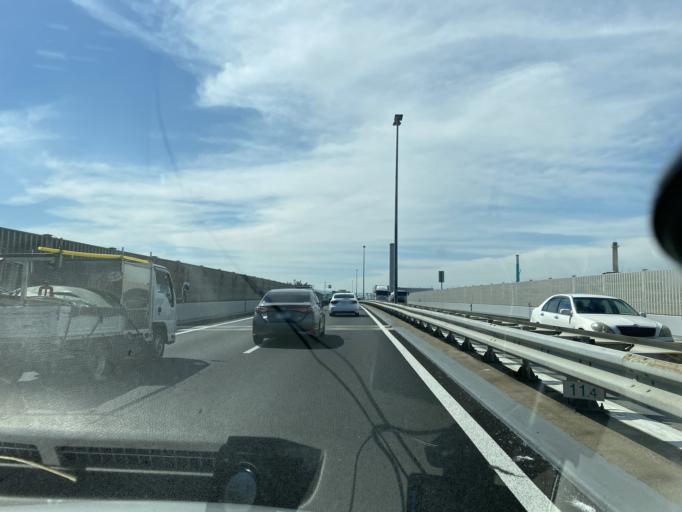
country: JP
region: Osaka
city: Kadoma
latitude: 34.7257
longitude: 135.5834
